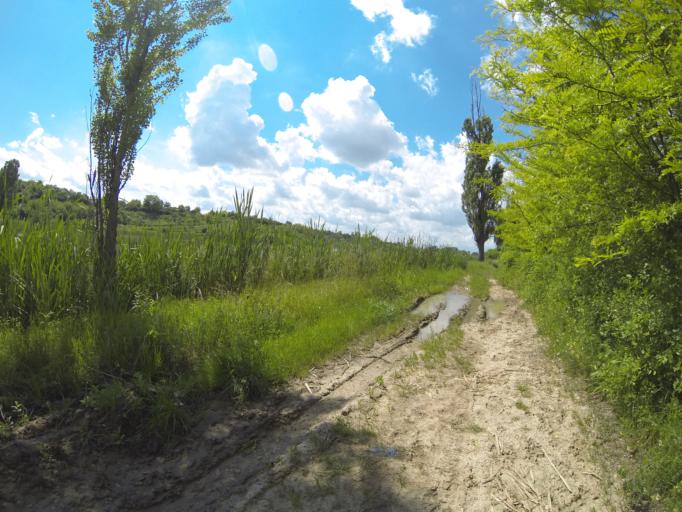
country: RO
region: Dolj
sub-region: Comuna Malu Mare
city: Preajba
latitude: 44.2665
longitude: 23.8547
